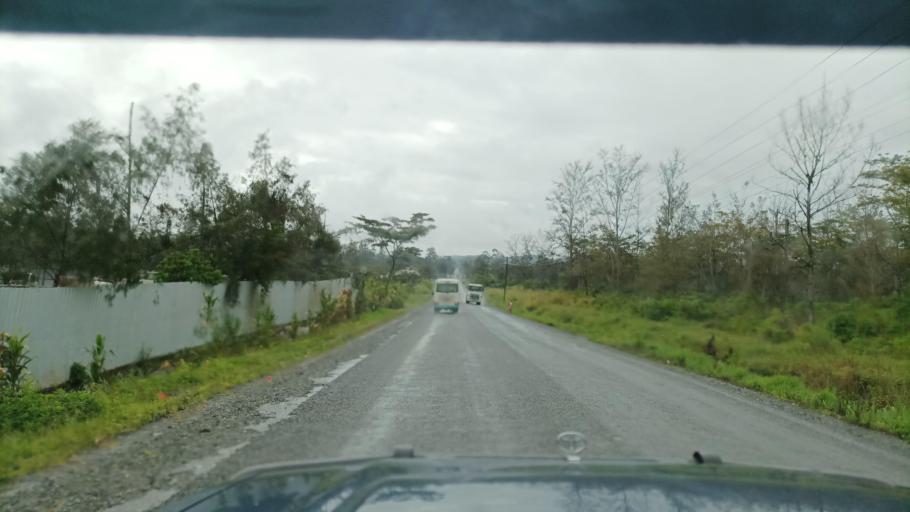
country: PG
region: Western Highlands
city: Rauna
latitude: -5.8249
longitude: 144.3798
